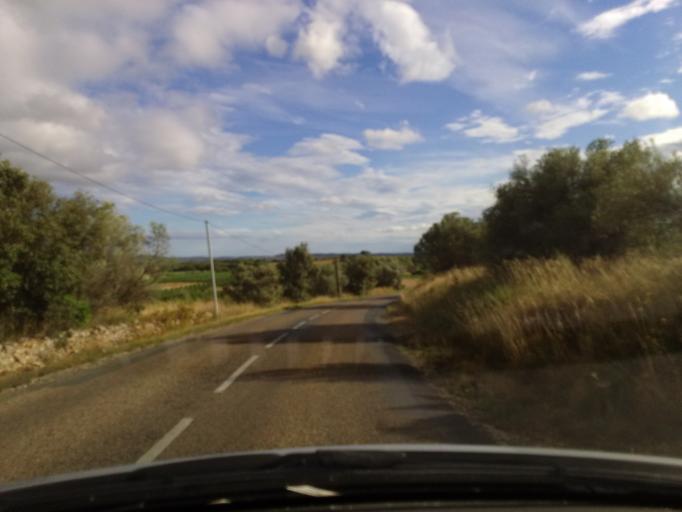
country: FR
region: Languedoc-Roussillon
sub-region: Departement de l'Herault
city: Saint-Jean-de-Fos
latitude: 43.6858
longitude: 3.5406
